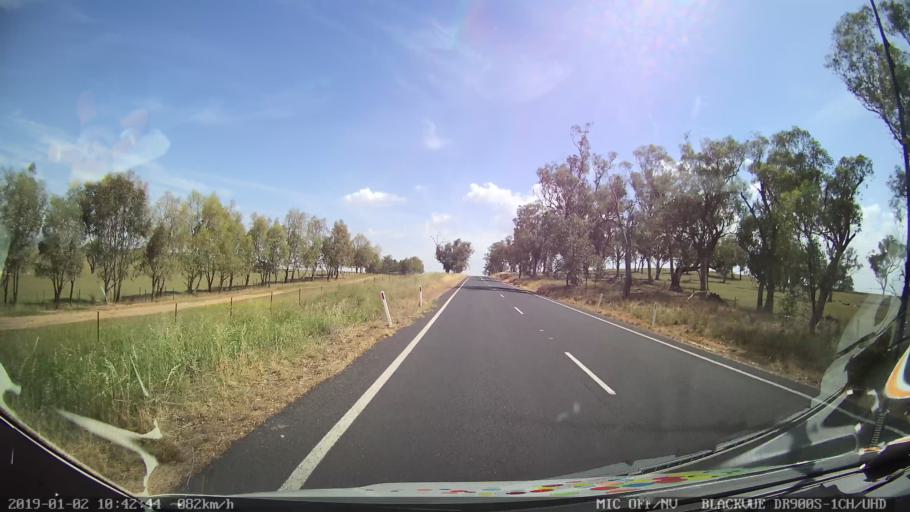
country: AU
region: New South Wales
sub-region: Cootamundra
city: Cootamundra
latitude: -34.7808
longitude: 148.3065
